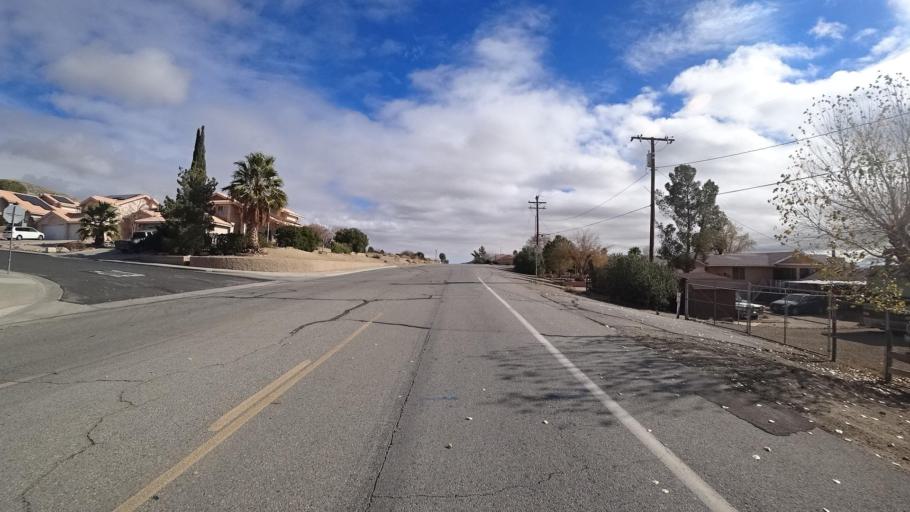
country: US
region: California
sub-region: Kern County
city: Rosamond
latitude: 34.8717
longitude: -118.1803
